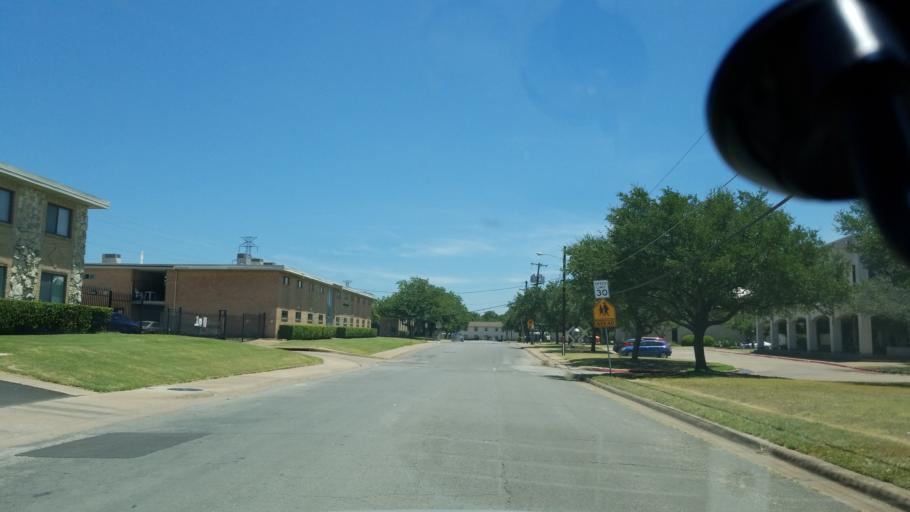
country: US
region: Texas
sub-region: Dallas County
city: Cockrell Hill
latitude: 32.7010
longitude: -96.8326
